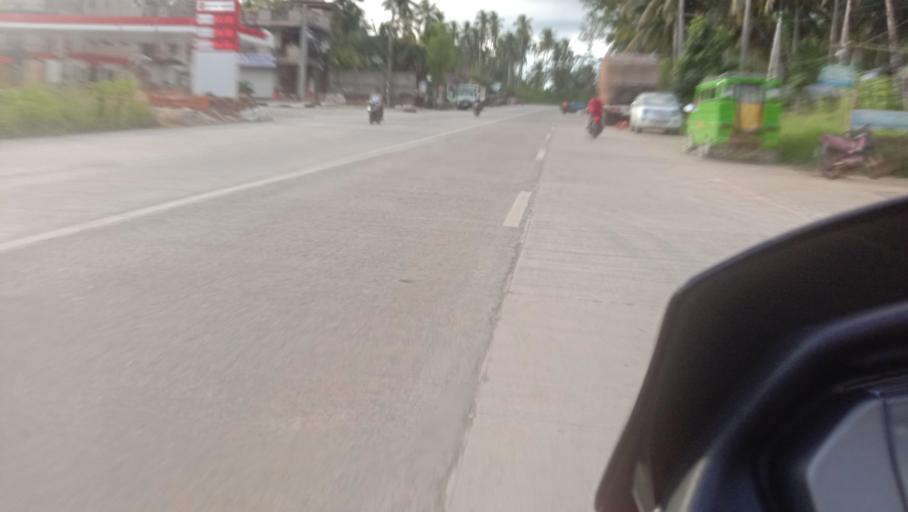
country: PH
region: Caraga
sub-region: Province of Surigao del Sur
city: Barobo
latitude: 8.5212
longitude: 126.1209
